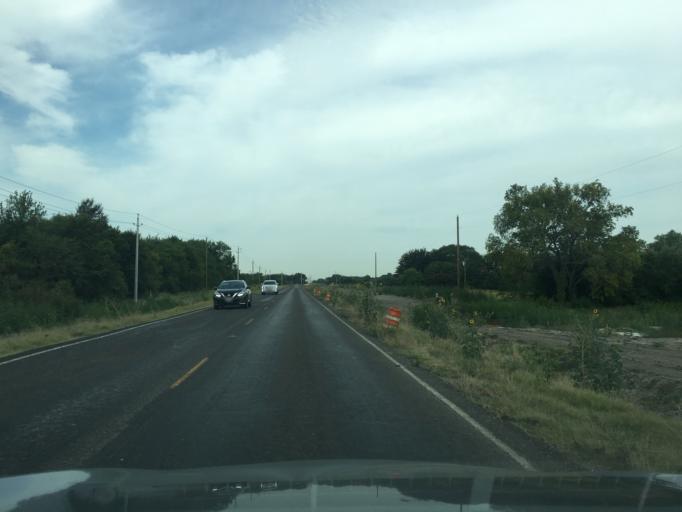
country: US
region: Texas
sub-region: Collin County
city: Lucas
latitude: 33.0550
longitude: -96.5877
